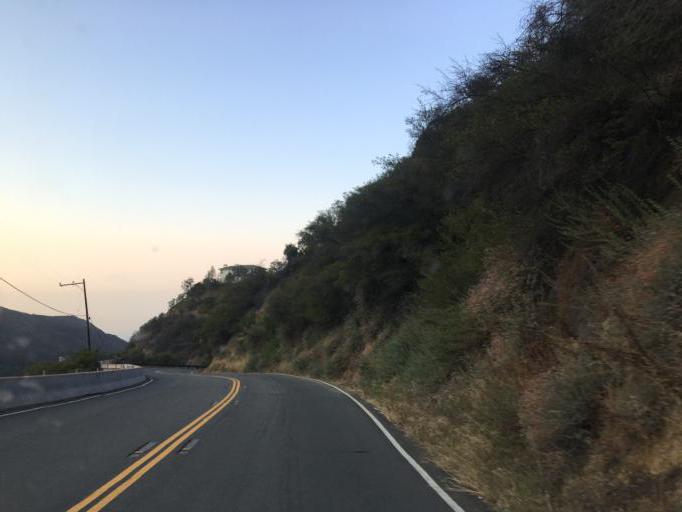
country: US
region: California
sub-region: Los Angeles County
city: Las Flores
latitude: 34.0659
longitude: -118.6406
